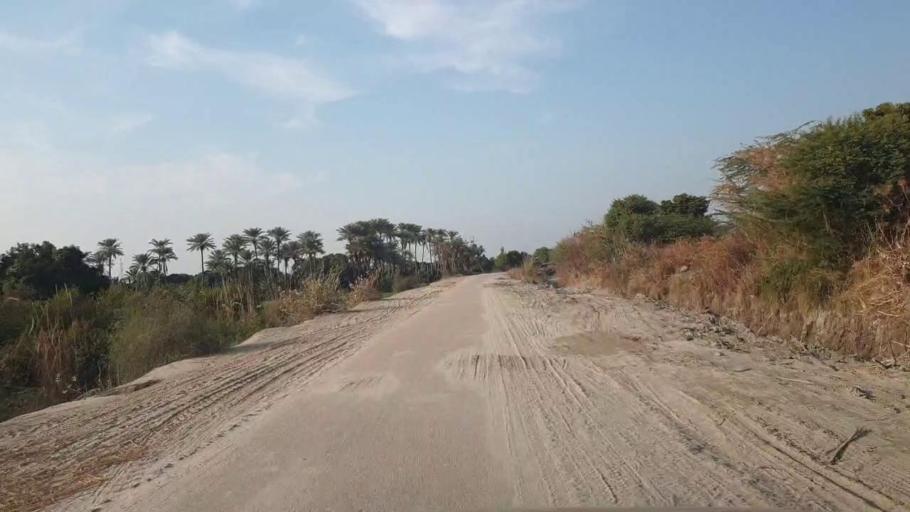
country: PK
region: Sindh
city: Shahpur Chakar
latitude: 26.1540
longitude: 68.6413
